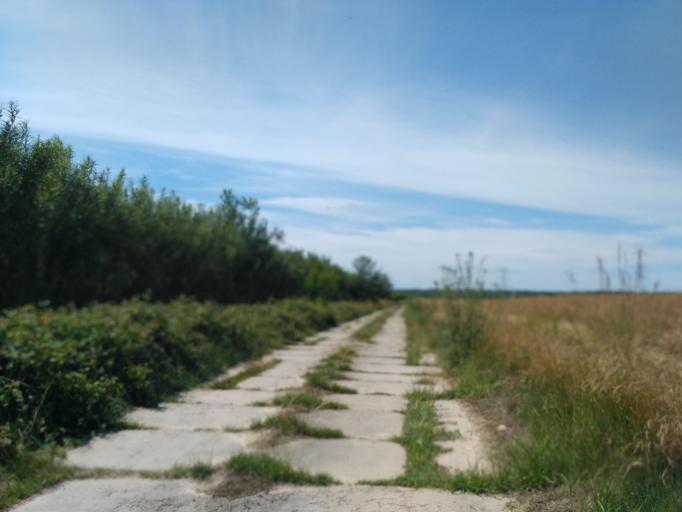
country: PL
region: Subcarpathian Voivodeship
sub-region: Powiat brzozowski
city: Haczow
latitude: 49.6538
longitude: 21.8658
